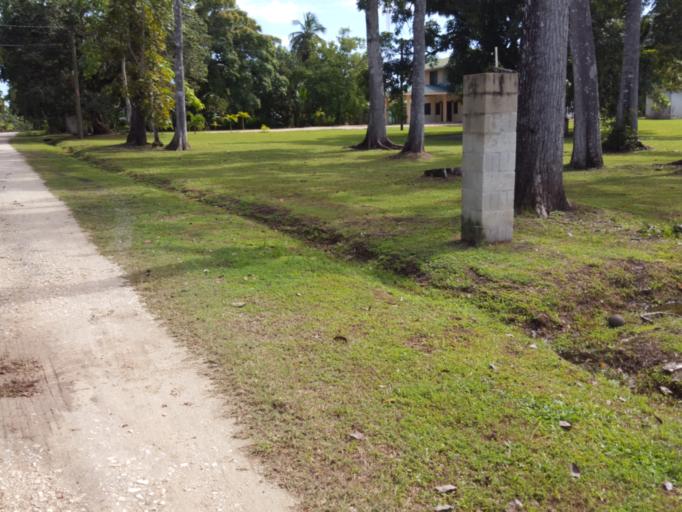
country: BZ
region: Belize
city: Belize City
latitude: 17.5708
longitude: -88.4059
